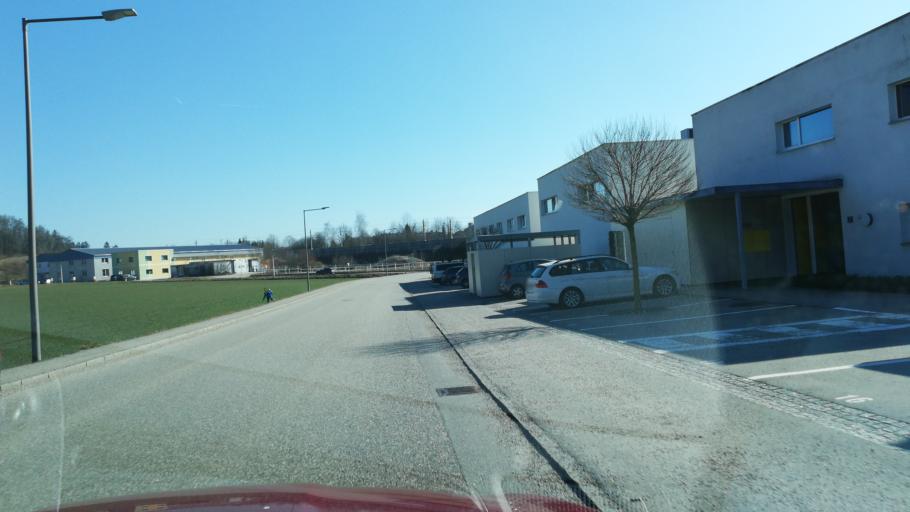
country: AT
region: Upper Austria
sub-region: Politischer Bezirk Vocklabruck
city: Schwanenstadt
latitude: 48.0618
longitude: 13.7757
